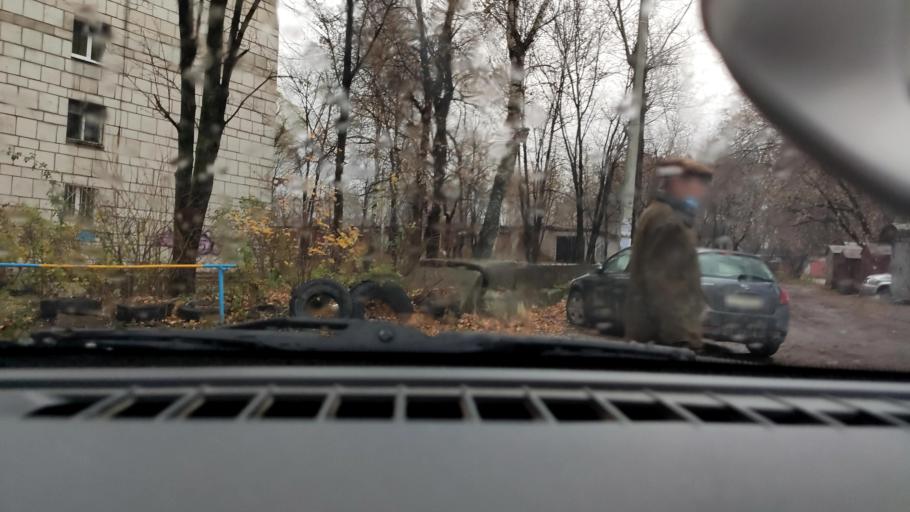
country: RU
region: Perm
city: Perm
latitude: 57.9887
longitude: 56.2317
